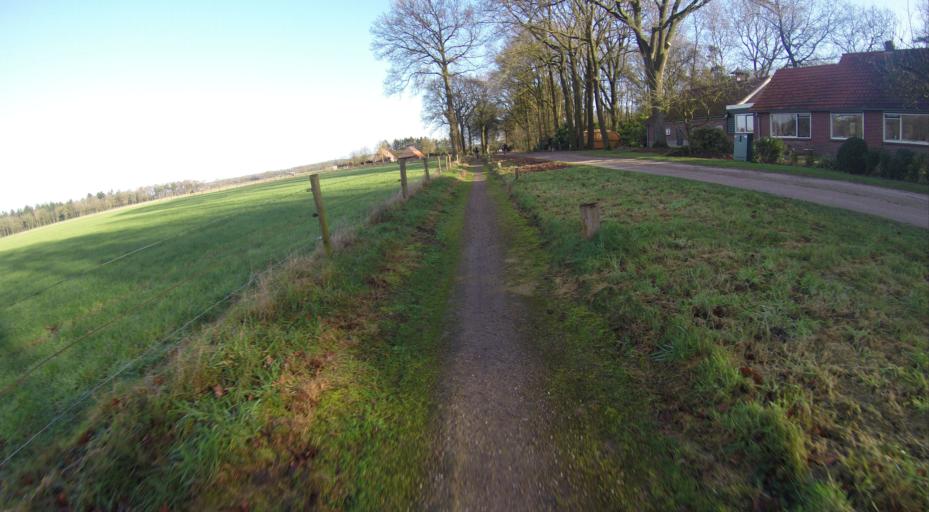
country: NL
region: Gelderland
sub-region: Gemeente Lochem
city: Laren
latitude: 52.3018
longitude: 6.3873
